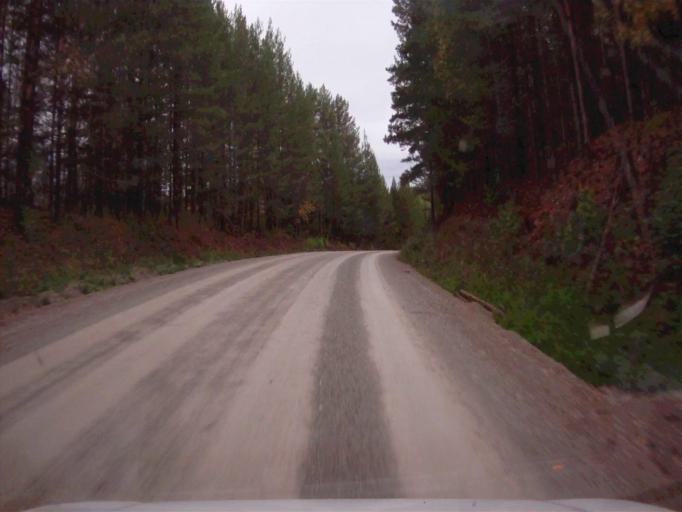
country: RU
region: Chelyabinsk
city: Nyazepetrovsk
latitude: 56.0585
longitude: 59.4547
